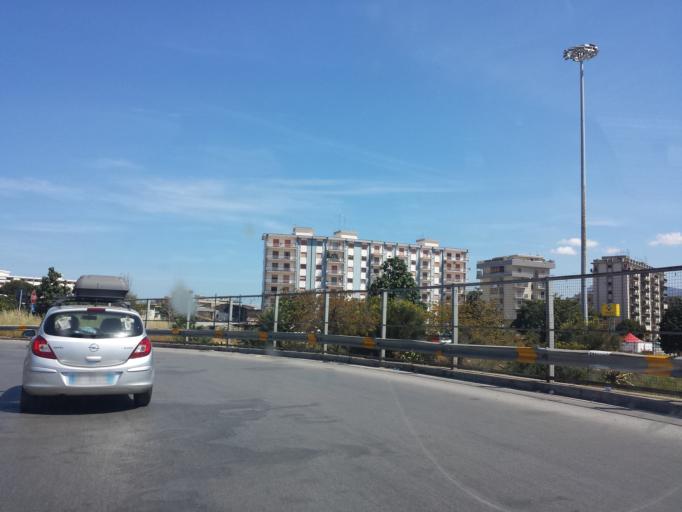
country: IT
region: Sicily
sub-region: Palermo
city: Palermo
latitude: 38.1392
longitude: 13.3310
